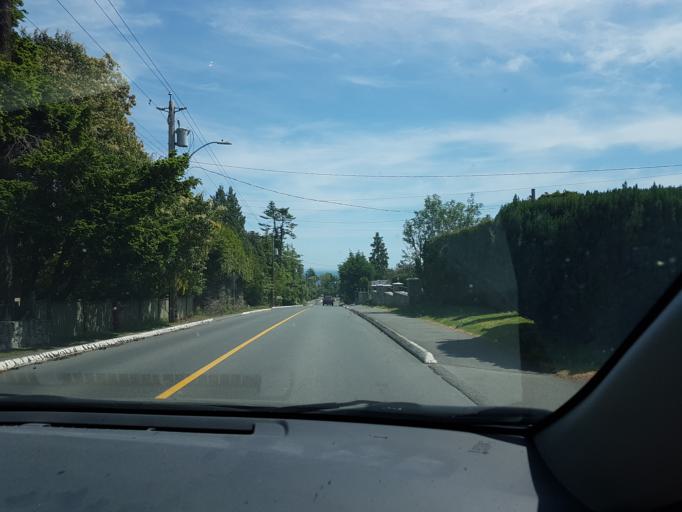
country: CA
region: British Columbia
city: Oak Bay
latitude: 48.4860
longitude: -123.3108
